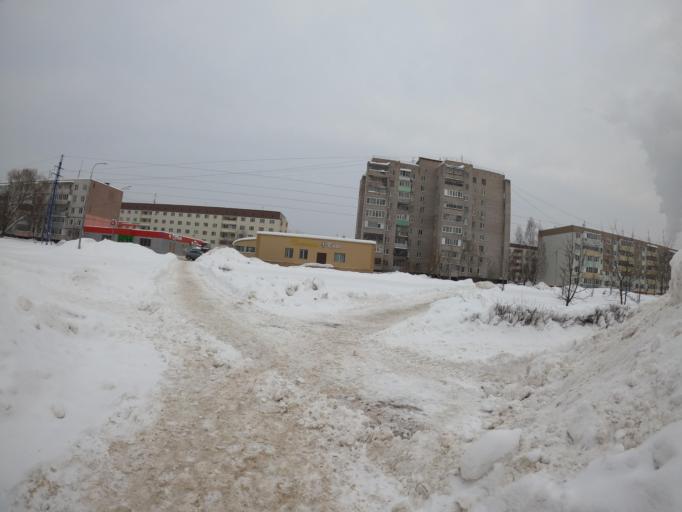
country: RU
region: Moskovskaya
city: Elektrogorsk
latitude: 55.8701
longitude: 38.7808
